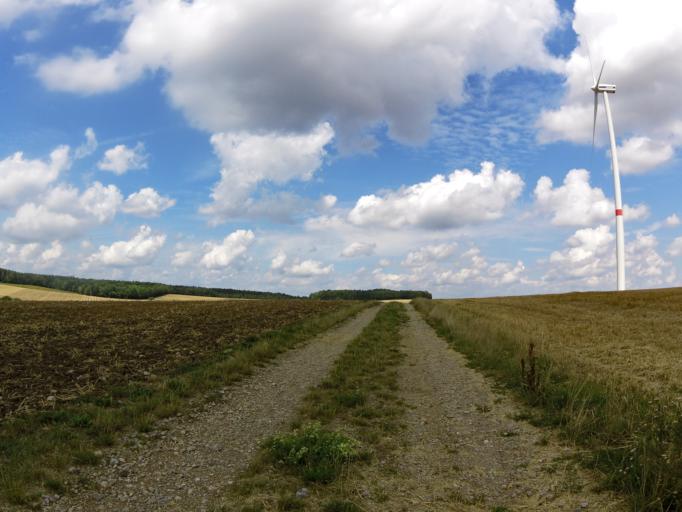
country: DE
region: Bavaria
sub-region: Regierungsbezirk Unterfranken
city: Geroldshausen
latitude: 49.6971
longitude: 9.8880
